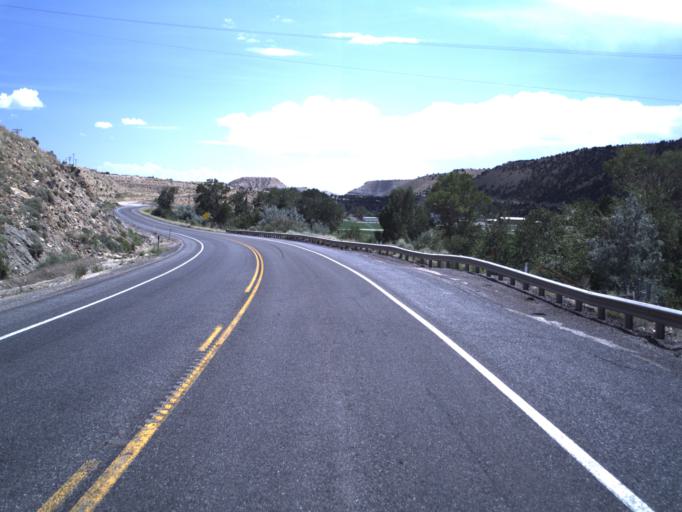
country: US
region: Utah
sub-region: Emery County
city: Huntington
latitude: 39.3769
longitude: -111.0689
